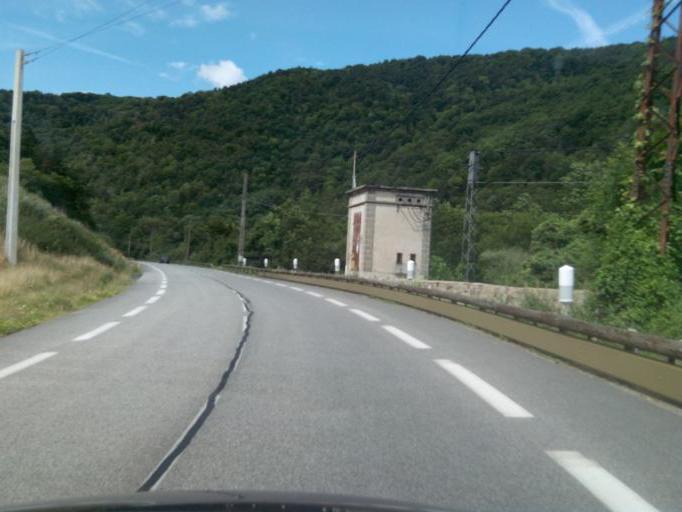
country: FR
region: Auvergne
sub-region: Departement de la Haute-Loire
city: Chadrac
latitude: 45.1113
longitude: 3.8947
